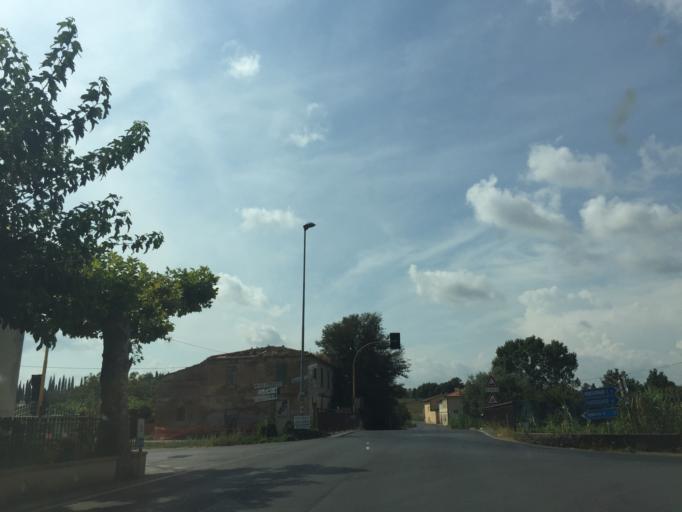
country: IT
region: Tuscany
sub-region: Province of Florence
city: Lazzeretto
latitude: 43.7780
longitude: 10.8623
